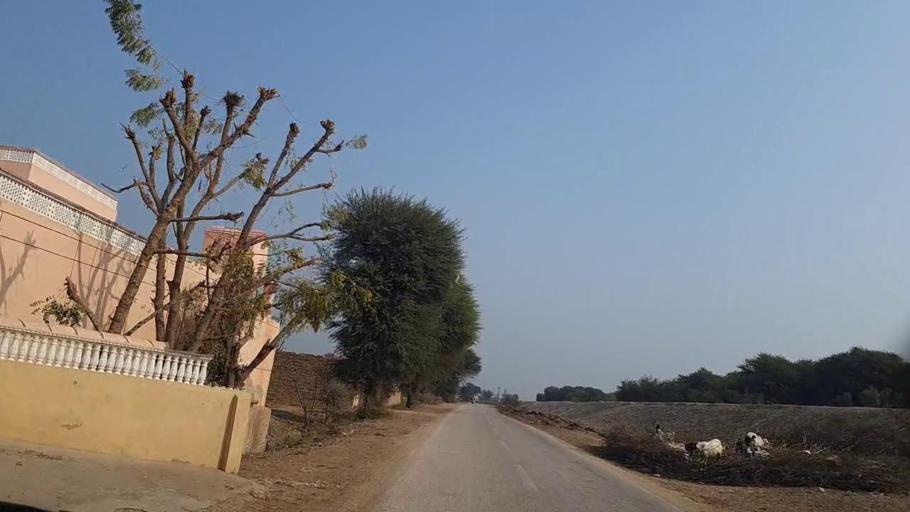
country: PK
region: Sindh
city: Sann
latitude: 26.1490
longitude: 68.1298
